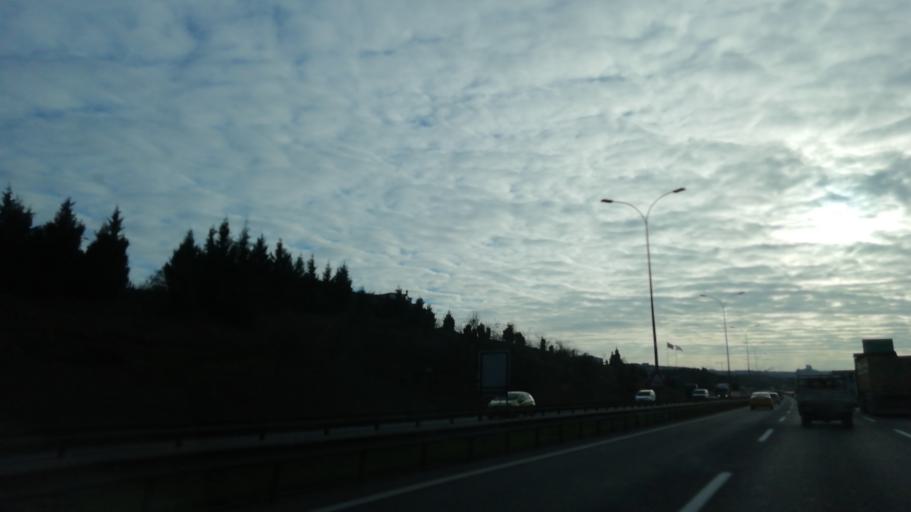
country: TR
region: Kocaeli
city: Balcik
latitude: 40.8786
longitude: 29.3842
